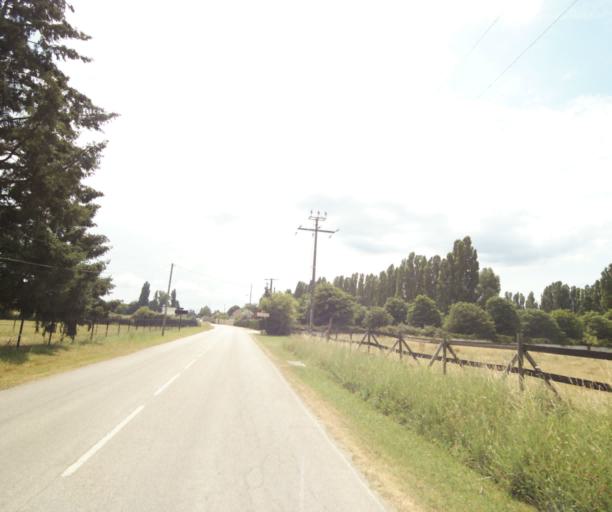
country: FR
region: Ile-de-France
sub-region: Departement de Seine-et-Marne
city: Barbizon
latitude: 48.4346
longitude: 2.5890
